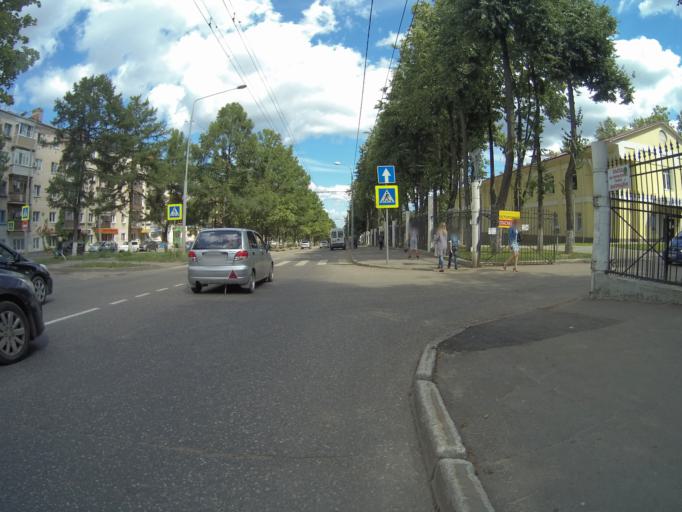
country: RU
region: Vladimir
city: Vladimir
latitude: 56.1436
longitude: 40.4131
